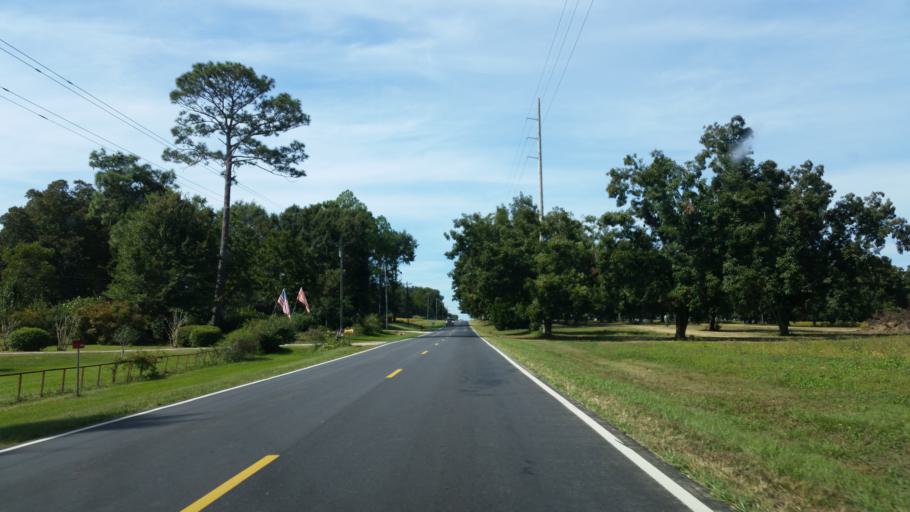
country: US
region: Alabama
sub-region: Baldwin County
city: Loxley
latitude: 30.6331
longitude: -87.7364
